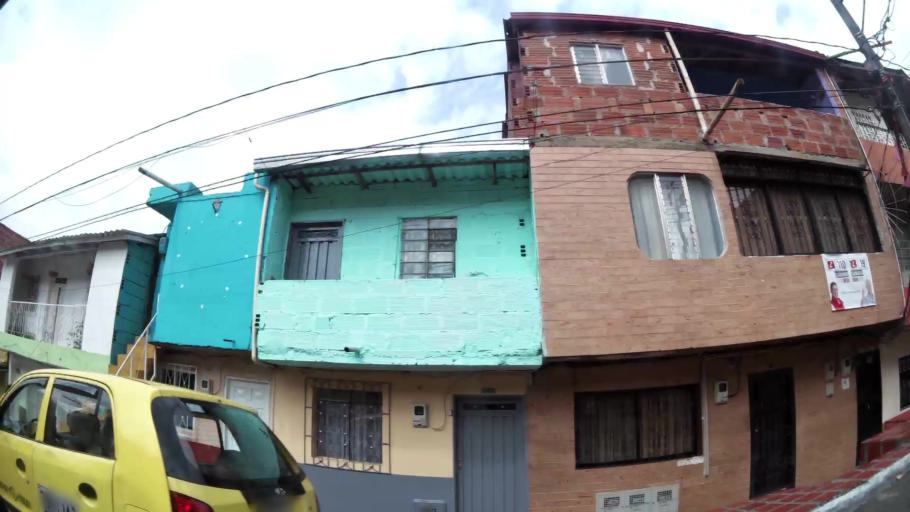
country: CO
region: Antioquia
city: Medellin
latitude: 6.2810
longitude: -75.5522
